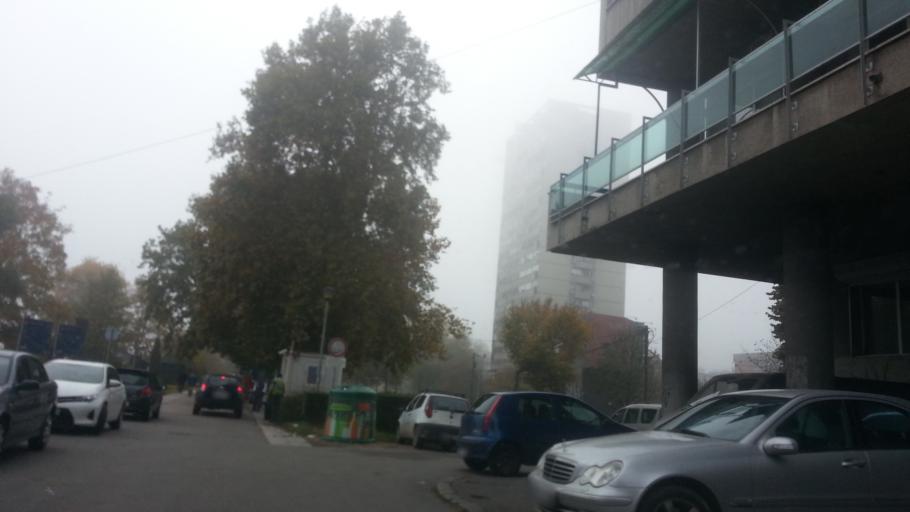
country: RS
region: Central Serbia
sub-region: Belgrade
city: Zemun
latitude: 44.8373
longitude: 20.4188
